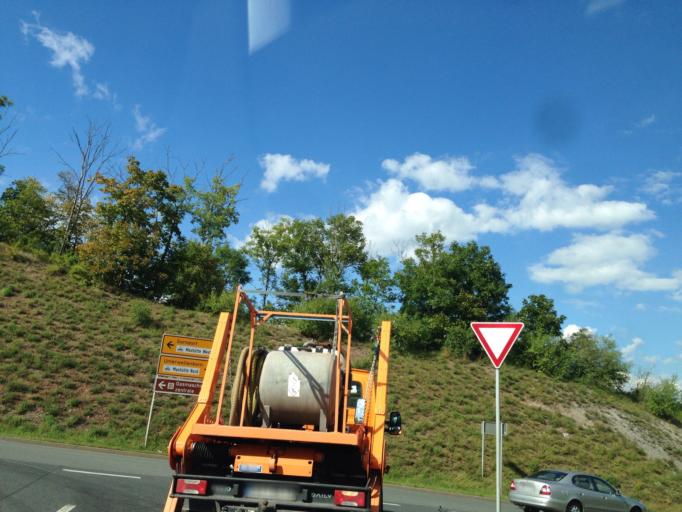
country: DE
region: Thuringia
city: Unterwellenborn
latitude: 50.6560
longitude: 11.4269
